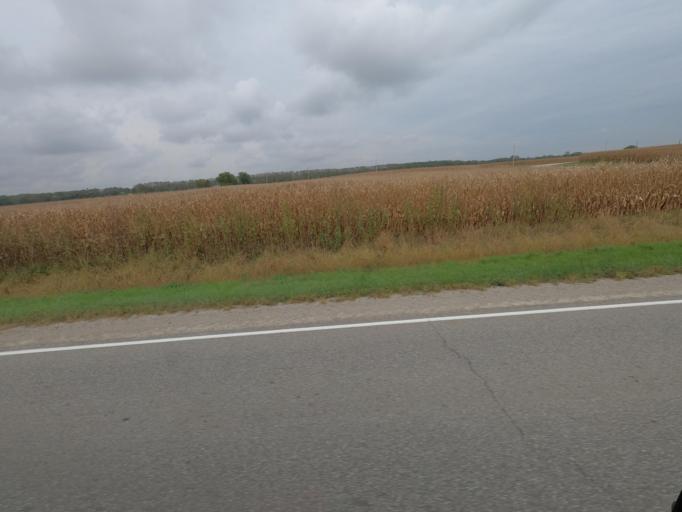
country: US
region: Iowa
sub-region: Wapello County
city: Ottumwa
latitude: 40.9064
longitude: -92.2043
